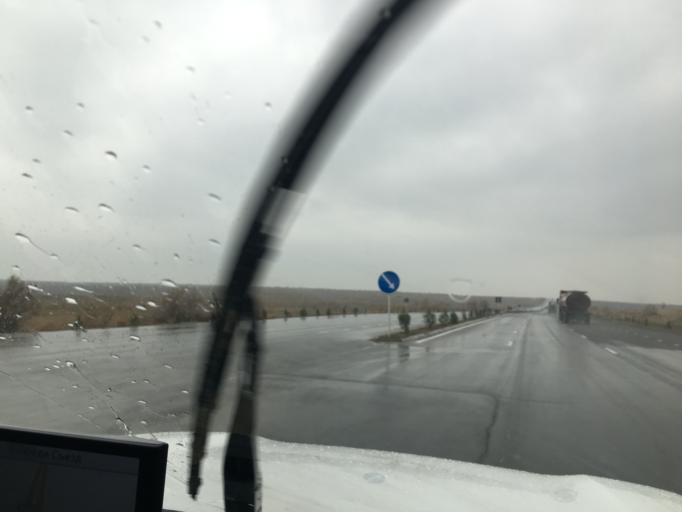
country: TM
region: Ahal
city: Annau
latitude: 37.8735
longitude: 58.6496
